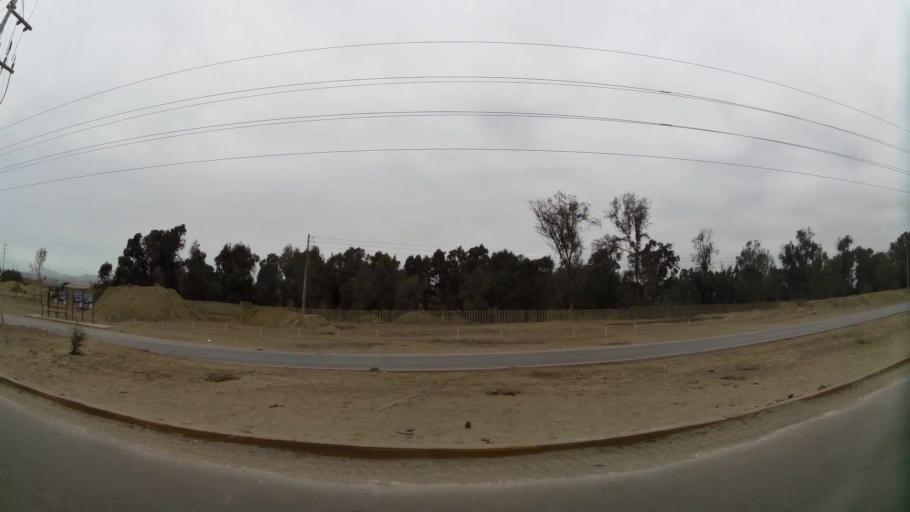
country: PE
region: Lima
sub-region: Lima
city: Surco
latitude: -12.2092
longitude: -76.9586
